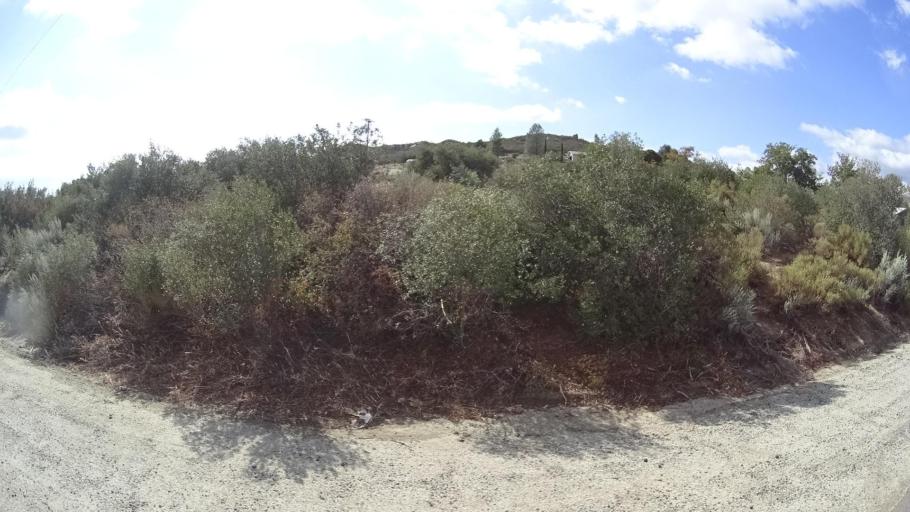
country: US
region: California
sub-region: San Diego County
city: Campo
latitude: 32.6880
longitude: -116.4885
